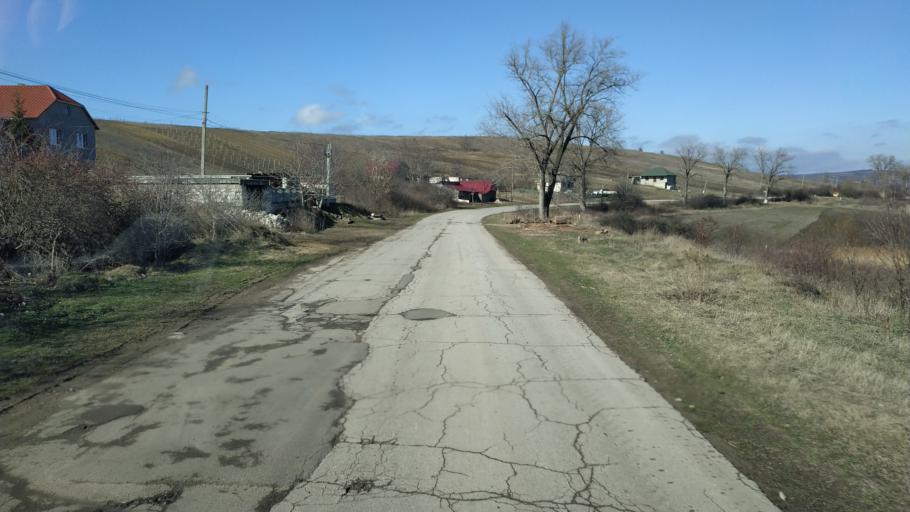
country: MD
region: Hincesti
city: Hincesti
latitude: 46.9770
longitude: 28.5717
